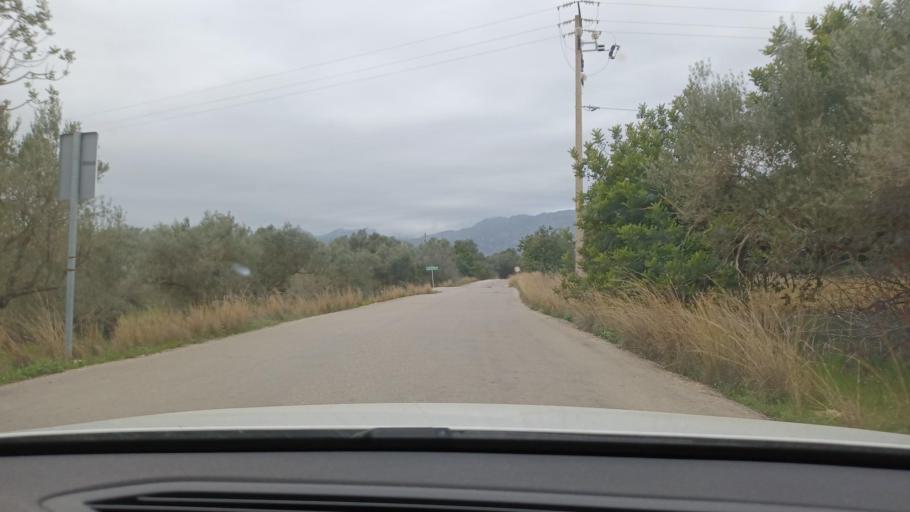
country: ES
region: Catalonia
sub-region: Provincia de Tarragona
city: Tortosa
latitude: 40.7953
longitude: 0.4514
